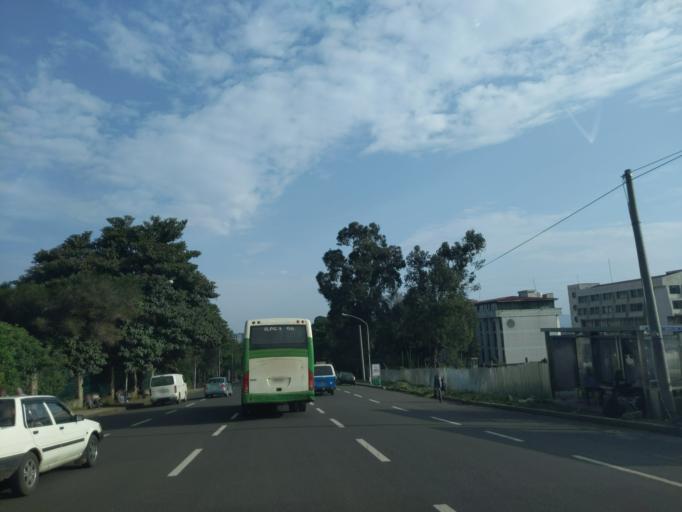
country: ET
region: Adis Abeba
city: Addis Ababa
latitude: 9.0214
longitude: 38.7636
